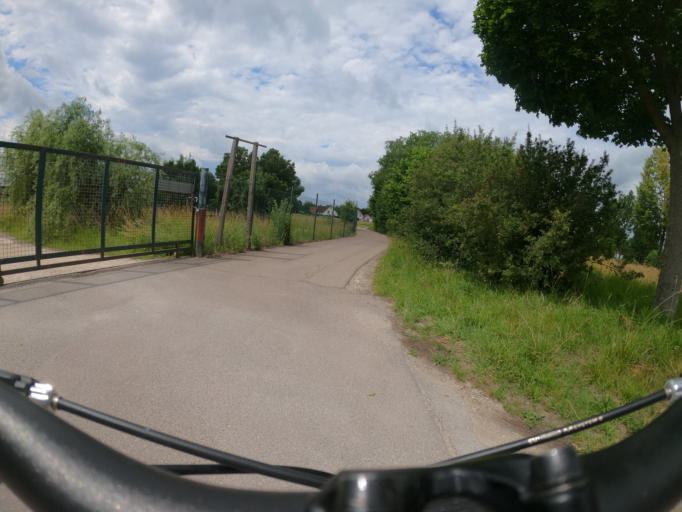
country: DE
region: Bavaria
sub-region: Swabia
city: Holzheim
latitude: 48.4207
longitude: 10.0732
